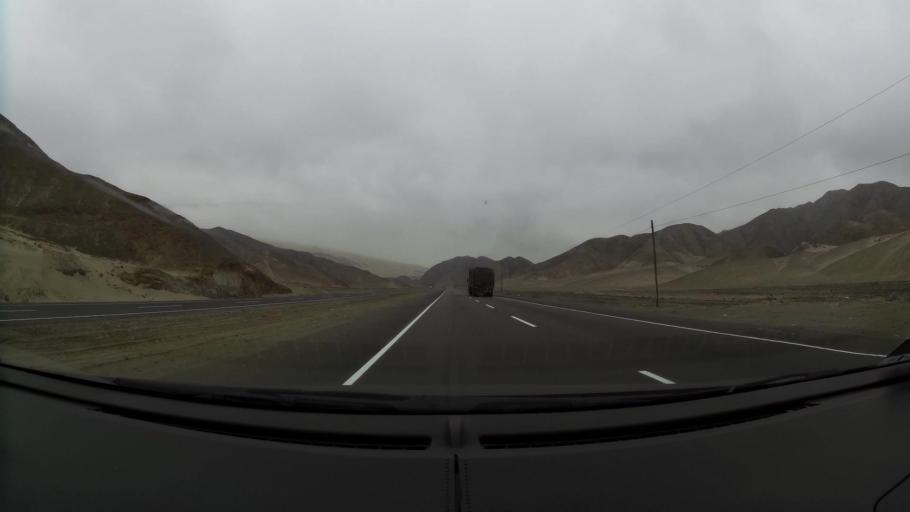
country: PE
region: La Libertad
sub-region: Viru
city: Chao
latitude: -8.7200
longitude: -78.6362
